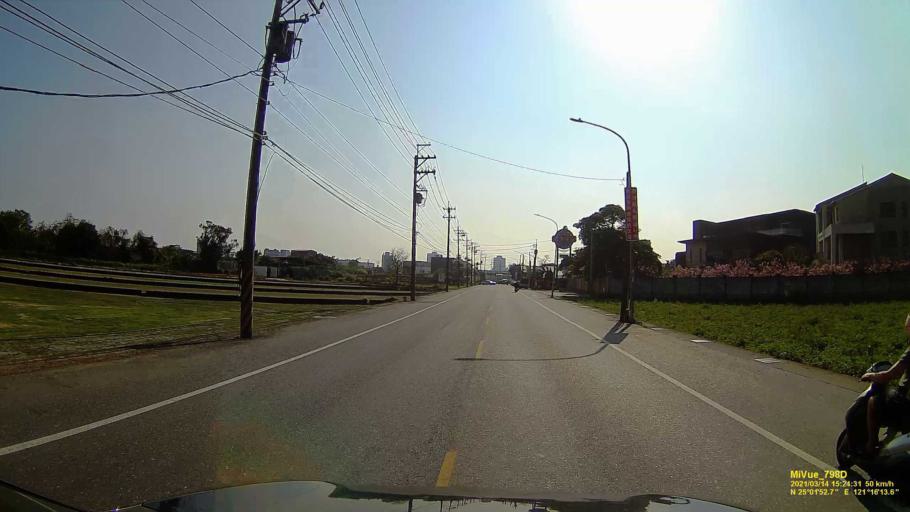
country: TW
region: Taiwan
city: Taoyuan City
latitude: 25.0311
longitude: 121.2702
